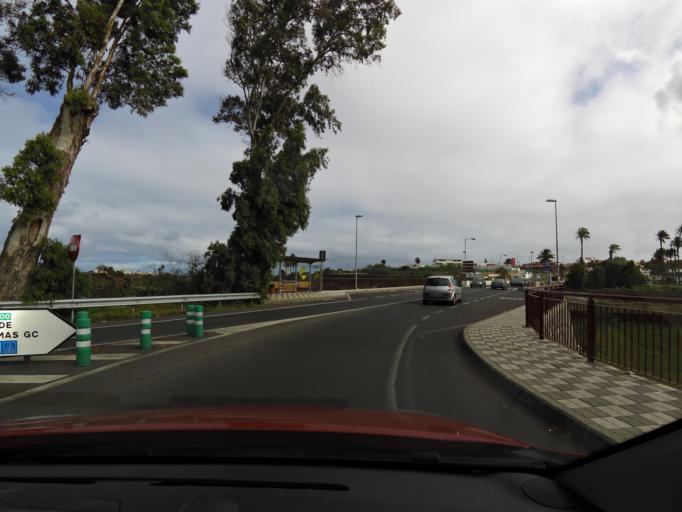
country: ES
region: Canary Islands
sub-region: Provincia de Las Palmas
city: Telde
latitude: 28.0073
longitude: -15.4176
